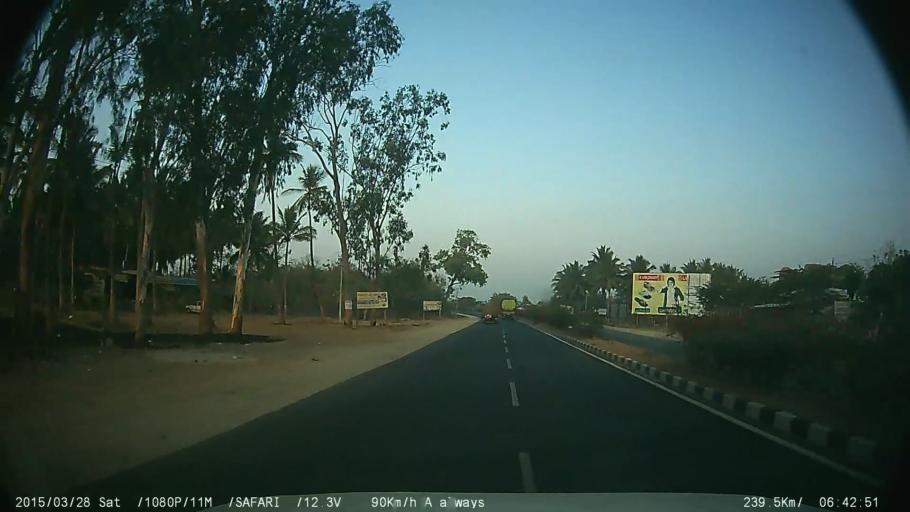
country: IN
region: Karnataka
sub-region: Ramanagara
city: Channapatna
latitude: 12.6358
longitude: 77.1247
